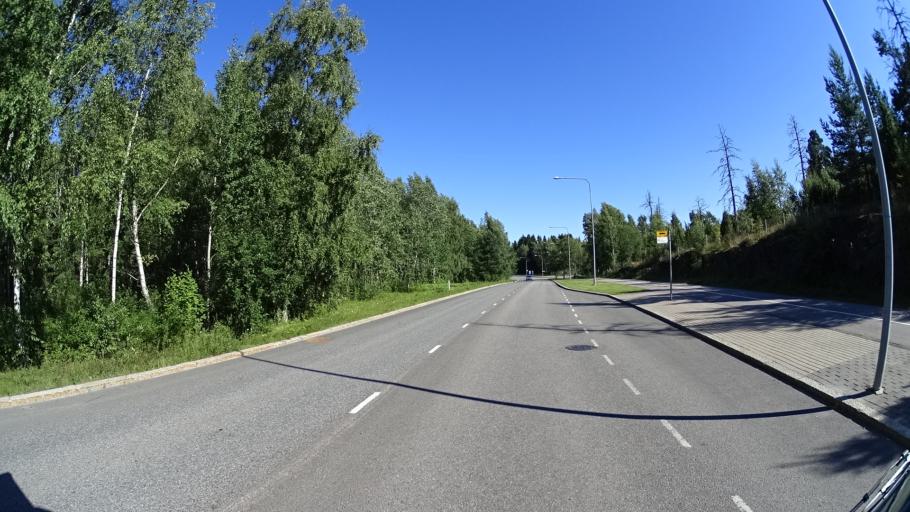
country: FI
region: Uusimaa
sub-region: Helsinki
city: Vantaa
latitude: 60.2224
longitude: 25.1504
